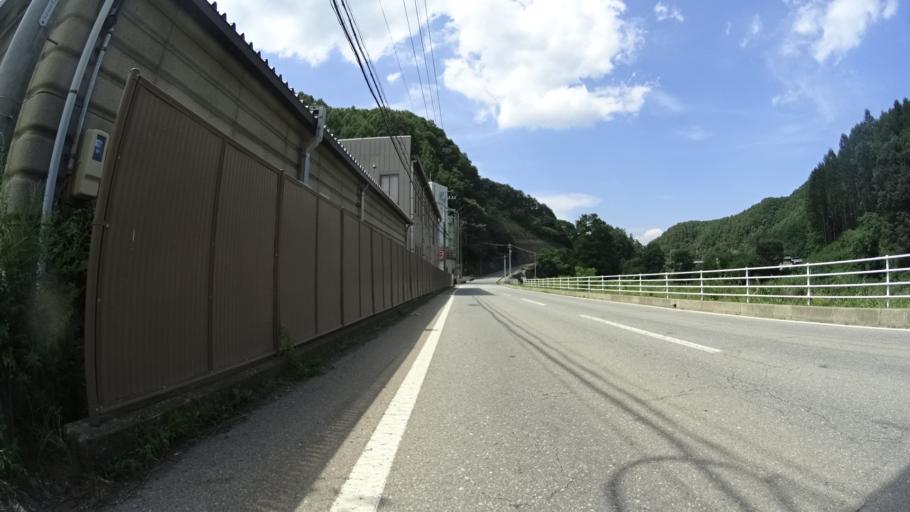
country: JP
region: Nagano
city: Saku
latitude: 36.0751
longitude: 138.4935
